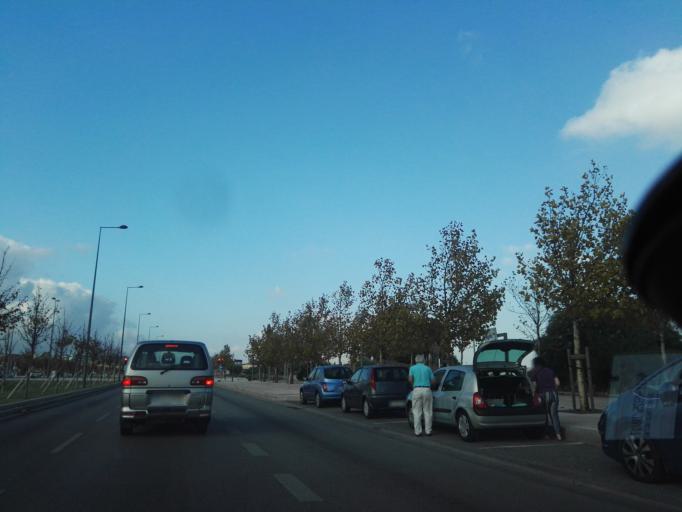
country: PT
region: Lisbon
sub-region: Odivelas
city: Olival do Basto
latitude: 38.7684
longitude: -9.1485
